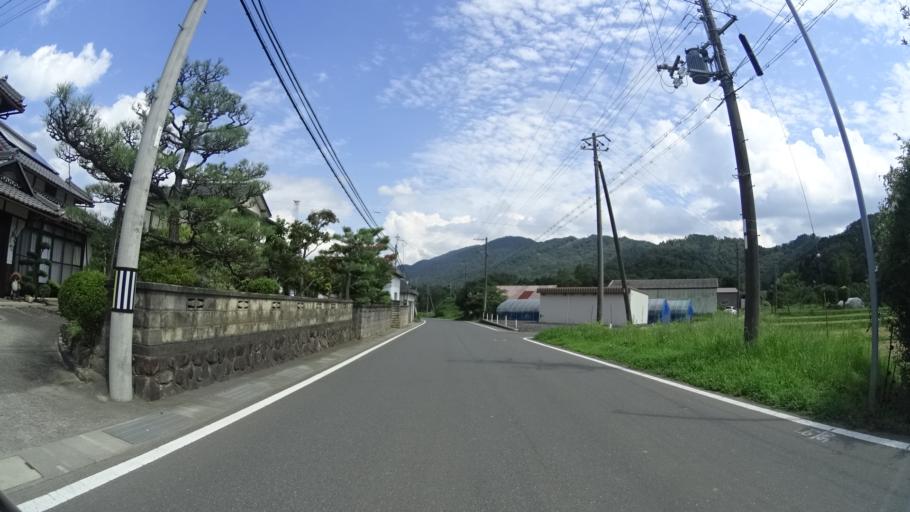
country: JP
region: Kyoto
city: Maizuru
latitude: 35.3647
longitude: 135.3235
